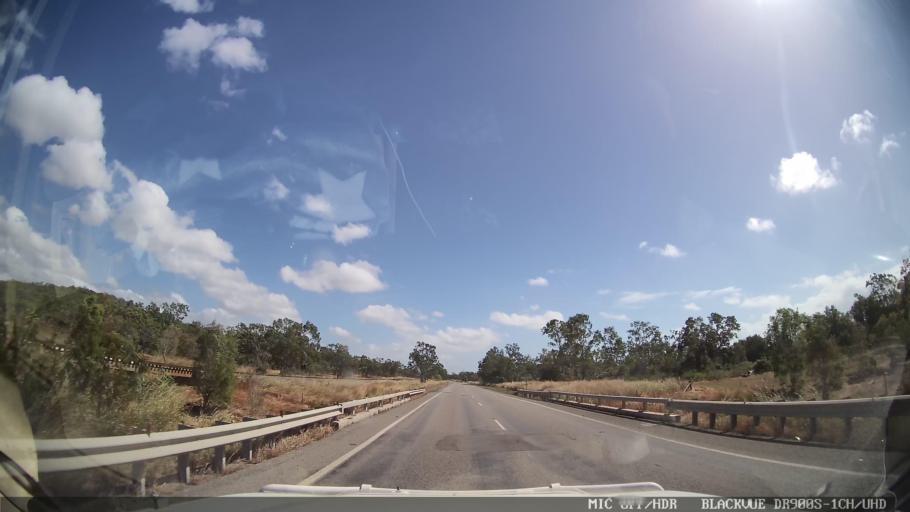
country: AU
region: Queensland
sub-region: Whitsunday
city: Bowen
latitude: -20.1806
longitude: 148.3505
